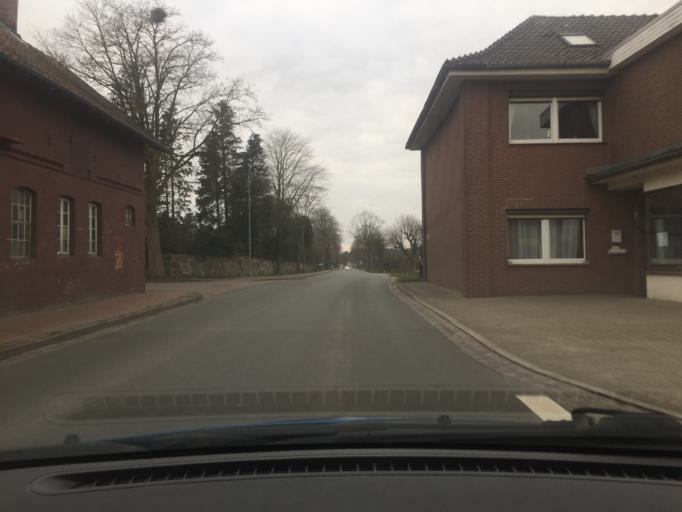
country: DE
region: Lower Saxony
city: Rosche
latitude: 52.9875
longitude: 10.7504
